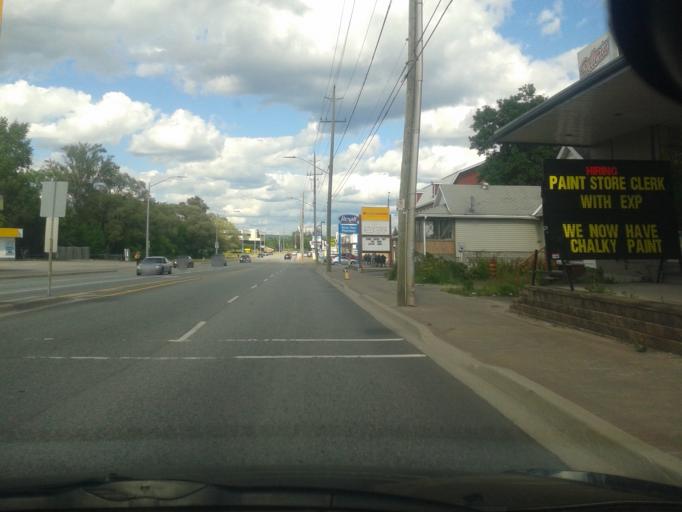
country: CA
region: Ontario
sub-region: Nipissing District
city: North Bay
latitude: 46.3109
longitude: -79.4496
